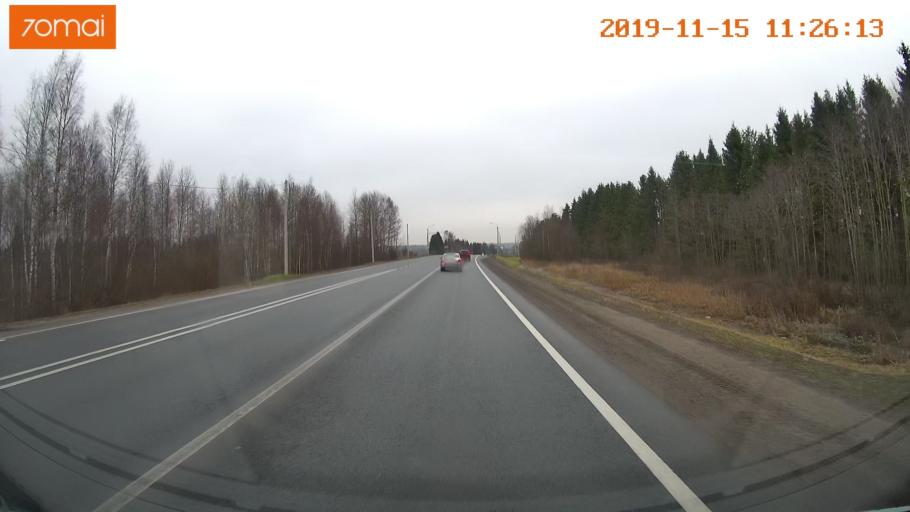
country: RU
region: Vologda
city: Molochnoye
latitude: 59.1659
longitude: 39.4408
